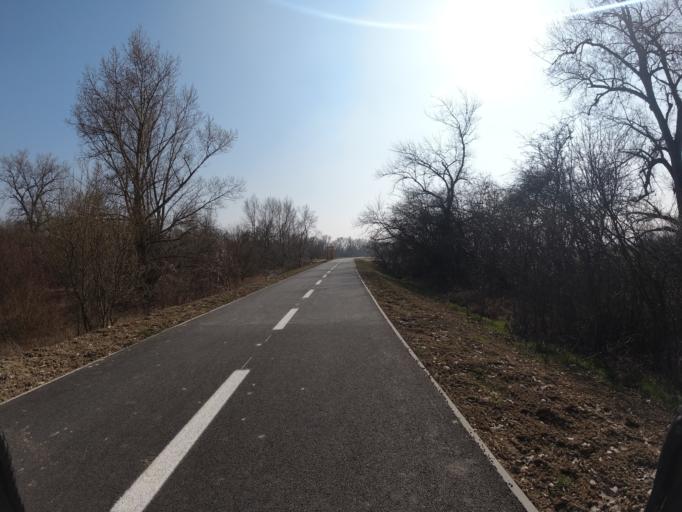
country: SK
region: Trenciansky
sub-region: Okres Nove Mesto nad Vahom
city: Nove Mesto nad Vahom
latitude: 48.7475
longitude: 17.8507
